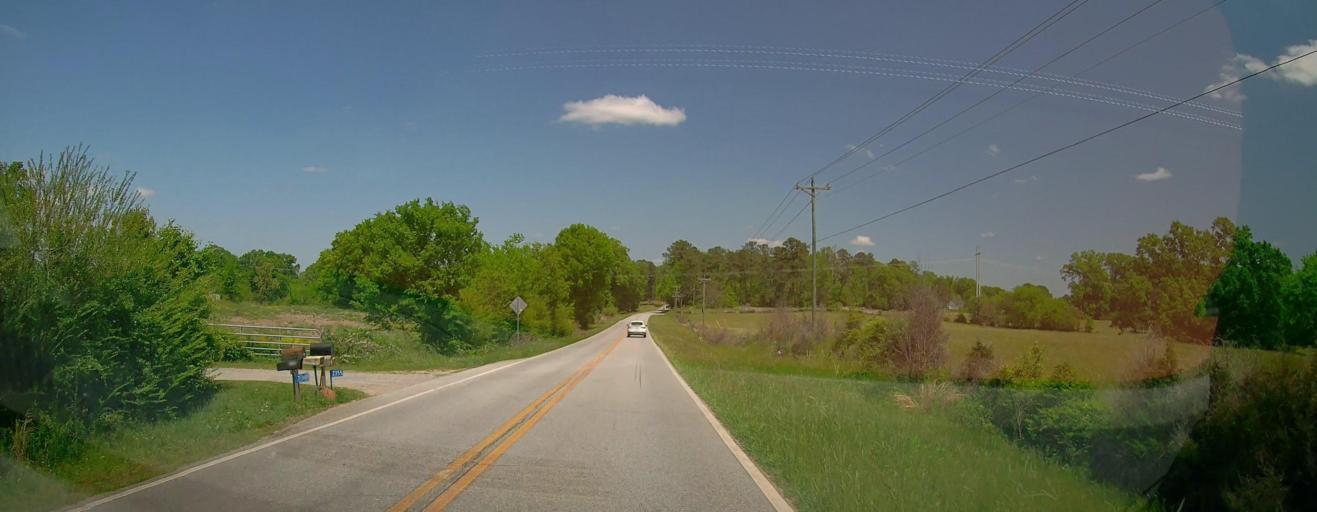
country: US
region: Georgia
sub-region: Bibb County
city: Macon
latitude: 32.9119
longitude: -83.6075
